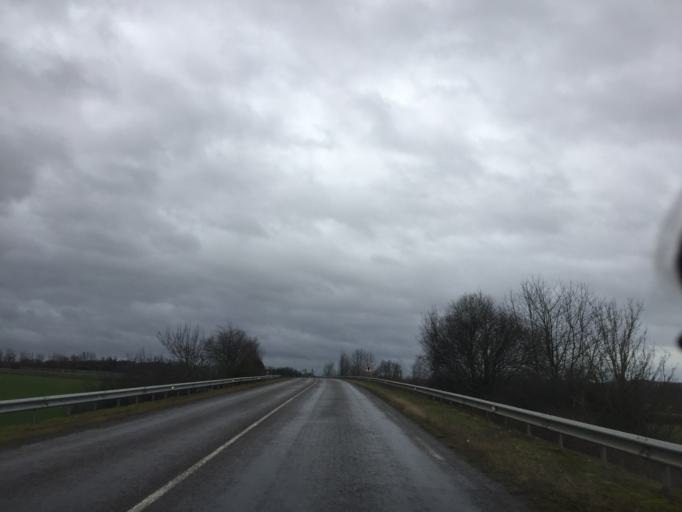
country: FR
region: Franche-Comte
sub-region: Departement du Jura
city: Dole
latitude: 47.1469
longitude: 5.5652
